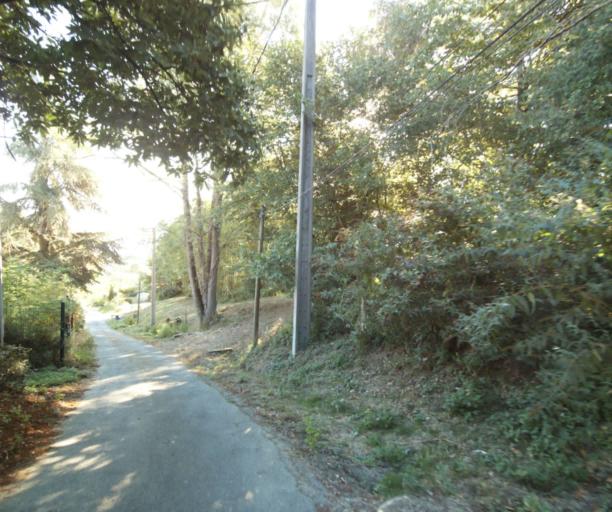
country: FR
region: Midi-Pyrenees
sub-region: Departement de la Haute-Garonne
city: Pechabou
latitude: 43.5075
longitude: 1.5029
